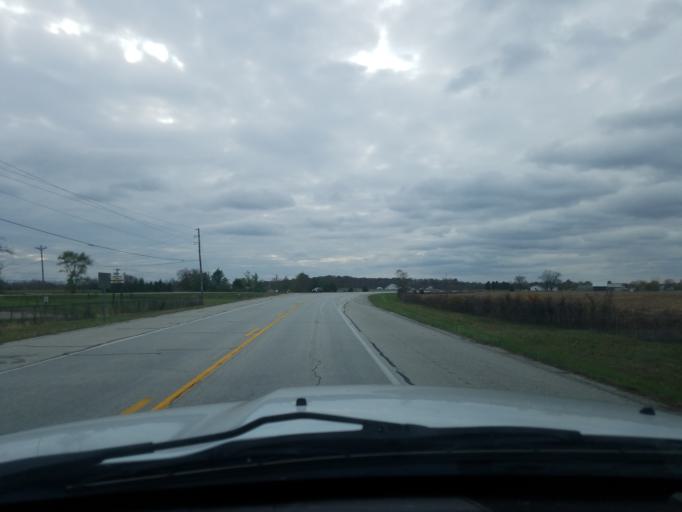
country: US
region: Indiana
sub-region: Bartholomew County
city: Hope
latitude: 39.1753
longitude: -85.7818
